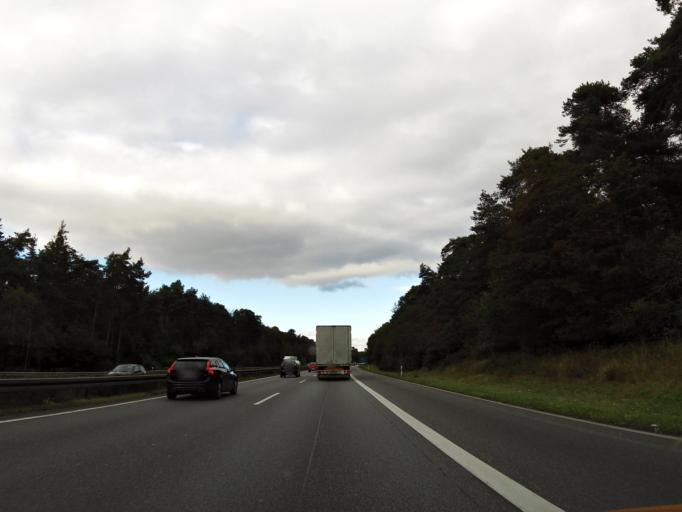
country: DE
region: Hesse
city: Raunheim
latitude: 49.9932
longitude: 8.4702
